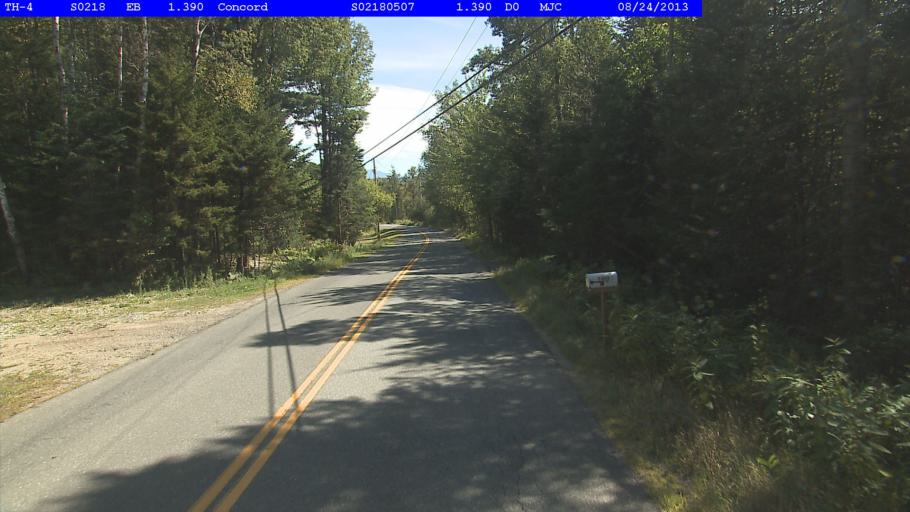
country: US
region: New Hampshire
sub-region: Grafton County
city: Littleton
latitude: 44.4463
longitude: -71.7656
